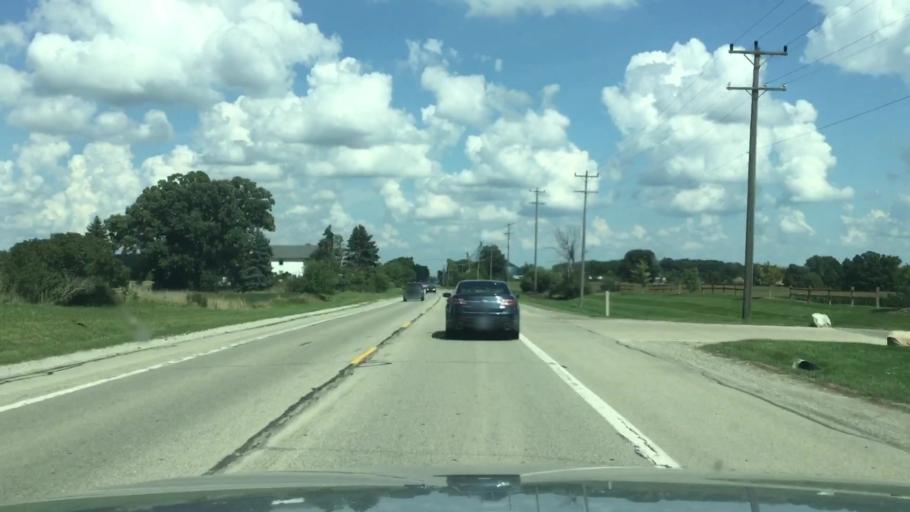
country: US
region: Michigan
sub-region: Washtenaw County
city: Saline
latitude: 42.1444
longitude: -83.8348
